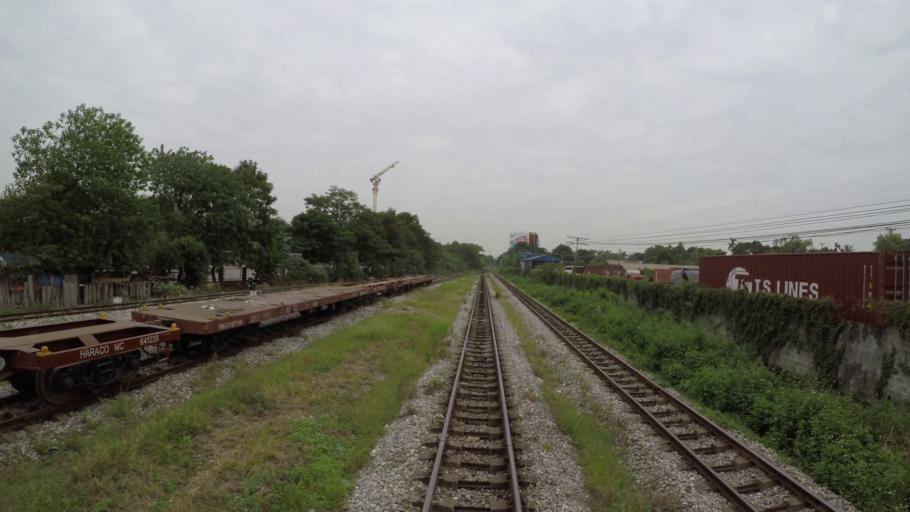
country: VN
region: Hai Phong
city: An Duong
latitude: 20.8792
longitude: 106.6252
